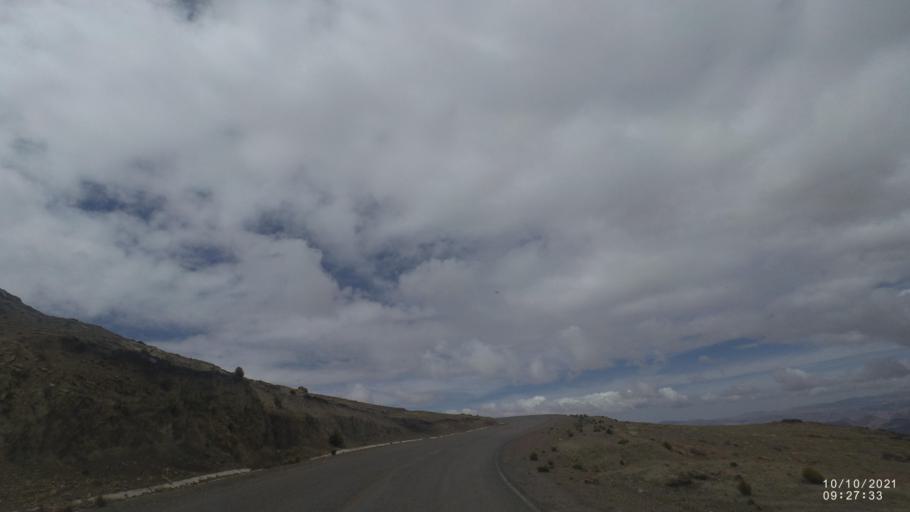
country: BO
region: La Paz
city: Quime
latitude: -17.1009
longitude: -67.3242
